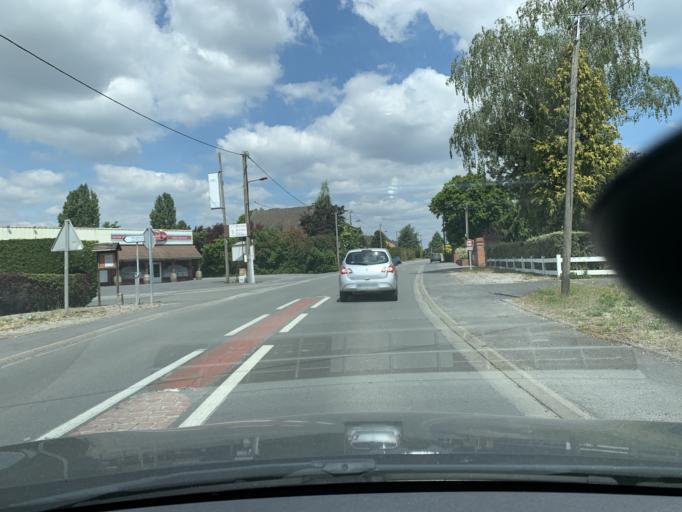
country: FR
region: Nord-Pas-de-Calais
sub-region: Departement du Nord
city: Goeulzin
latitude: 50.3217
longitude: 3.0948
